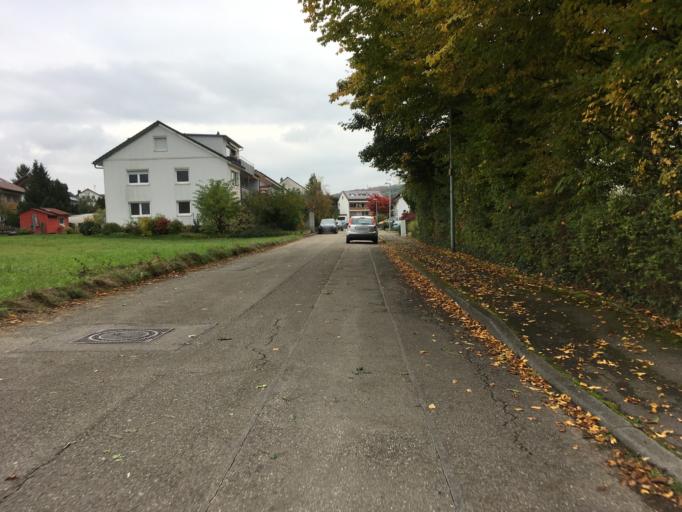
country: DE
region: Baden-Wuerttemberg
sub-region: Tuebingen Region
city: Gomaringen
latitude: 48.4500
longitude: 9.0960
